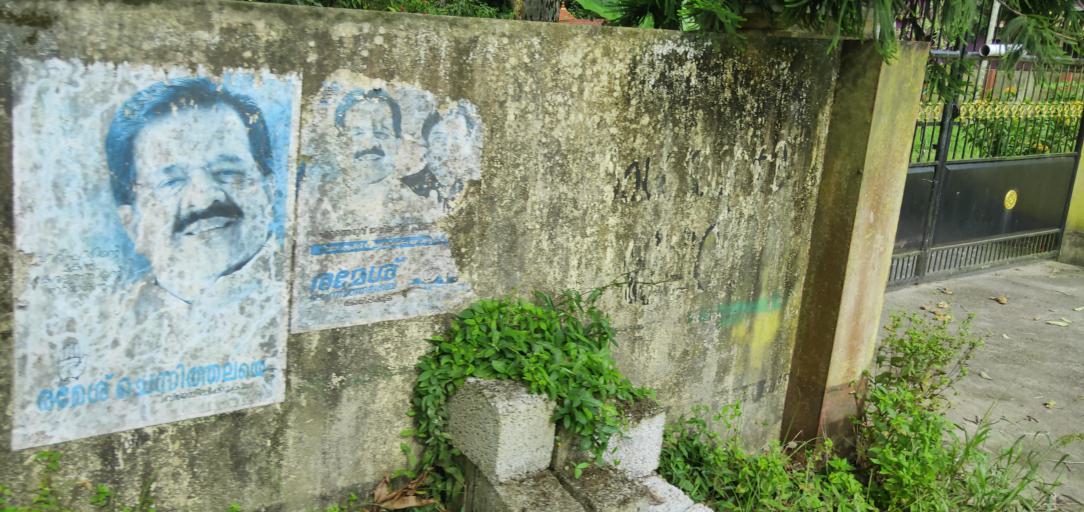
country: IN
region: Kerala
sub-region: Alappuzha
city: Kayankulam
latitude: 9.2323
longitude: 76.4570
